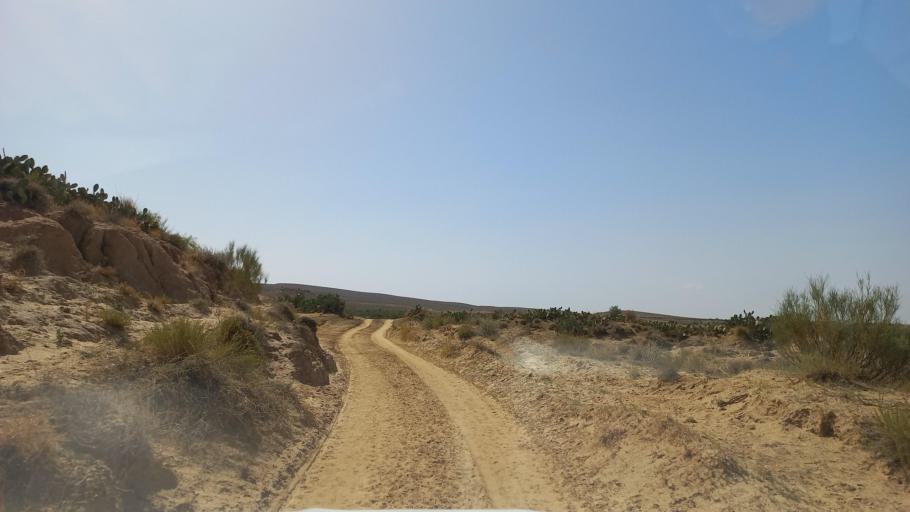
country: TN
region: Al Qasrayn
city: Kasserine
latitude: 35.1994
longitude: 9.0321
